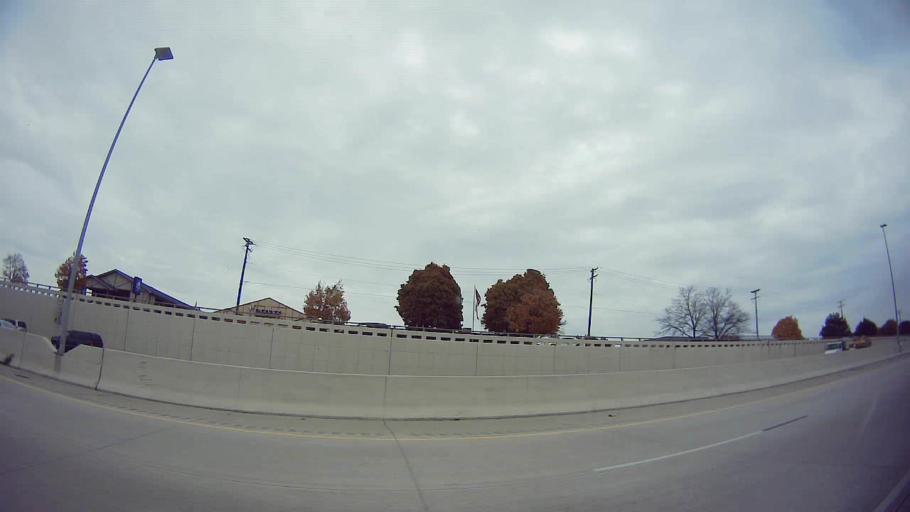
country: US
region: Michigan
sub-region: Wayne County
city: Redford
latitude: 42.3837
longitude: -83.3247
